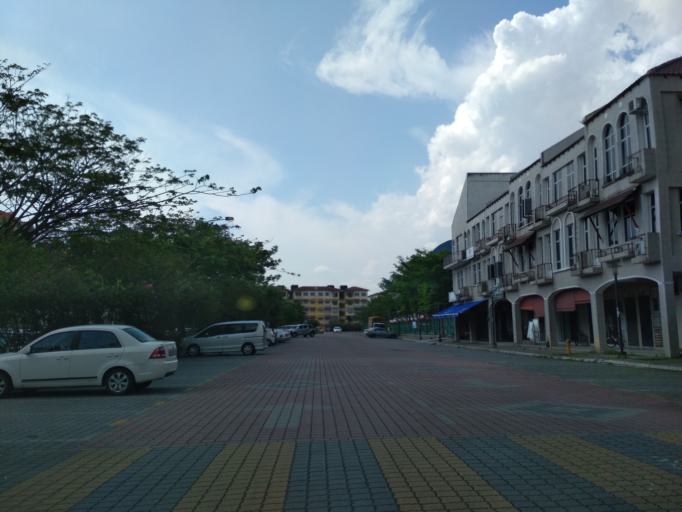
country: MY
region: Perak
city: Kampar
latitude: 4.3277
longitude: 101.1449
